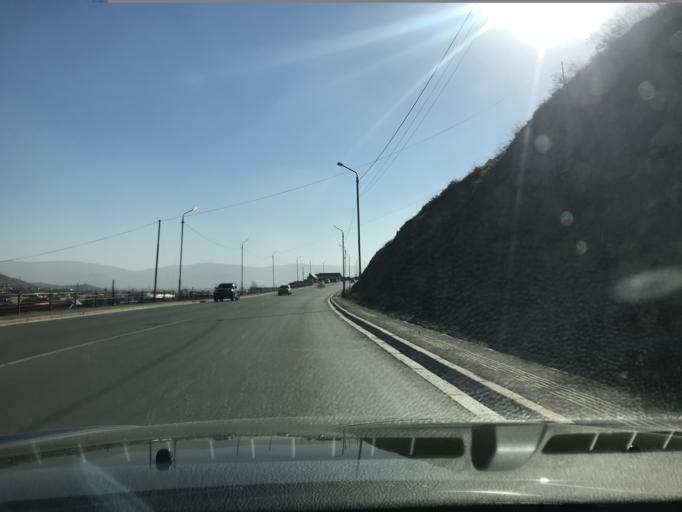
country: MN
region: Ulaanbaatar
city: Ulaanbaatar
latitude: 47.9861
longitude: 106.9248
